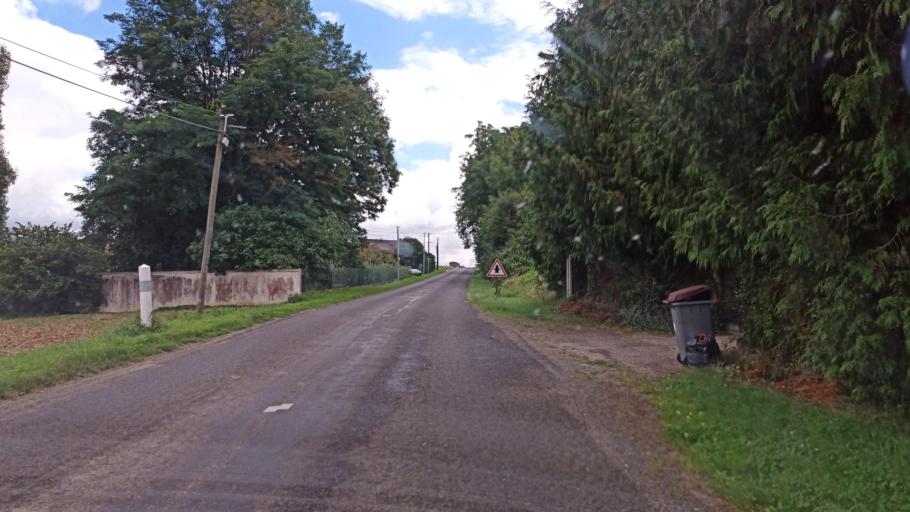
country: FR
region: Bourgogne
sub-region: Departement de l'Yonne
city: Cheroy
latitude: 48.2526
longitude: 3.0276
